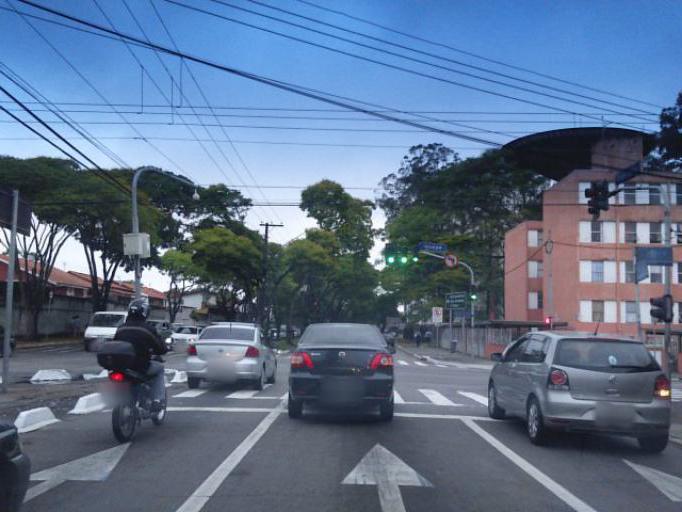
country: BR
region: Sao Paulo
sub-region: Sao Jose Dos Campos
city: Sao Jose dos Campos
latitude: -23.2353
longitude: -45.8806
